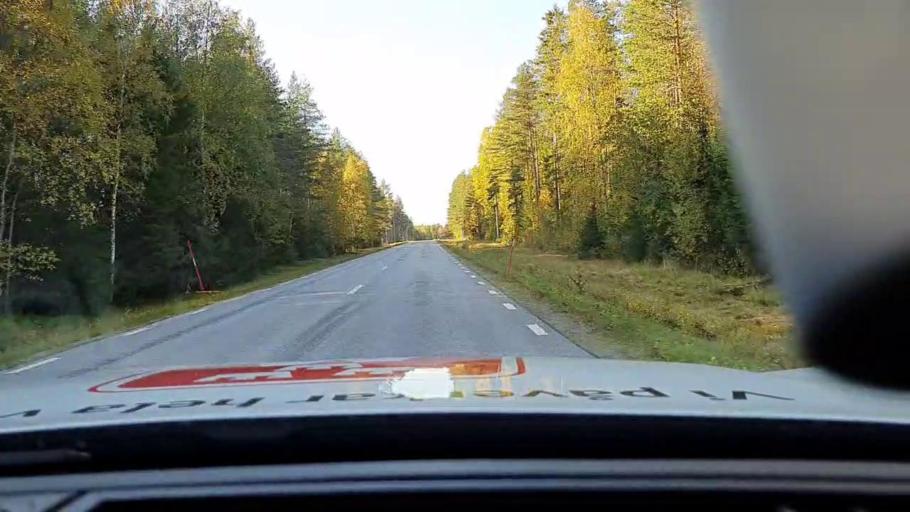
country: SE
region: Norrbotten
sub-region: Pitea Kommun
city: Norrfjarden
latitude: 65.4360
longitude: 21.4783
